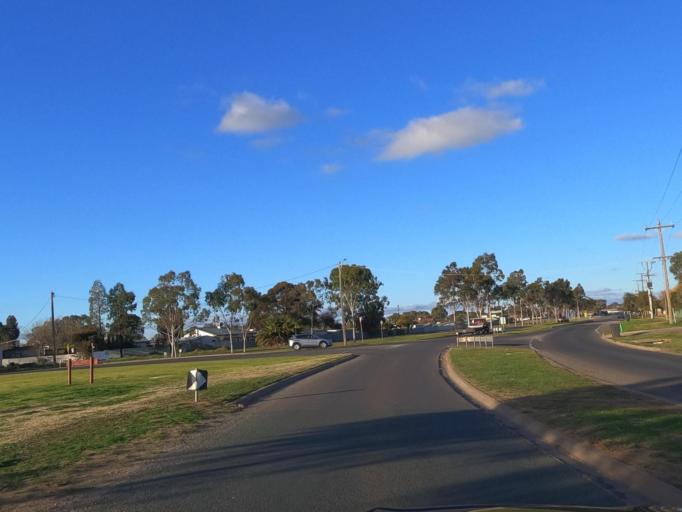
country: AU
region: Victoria
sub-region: Swan Hill
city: Swan Hill
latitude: -35.3398
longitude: 143.5398
